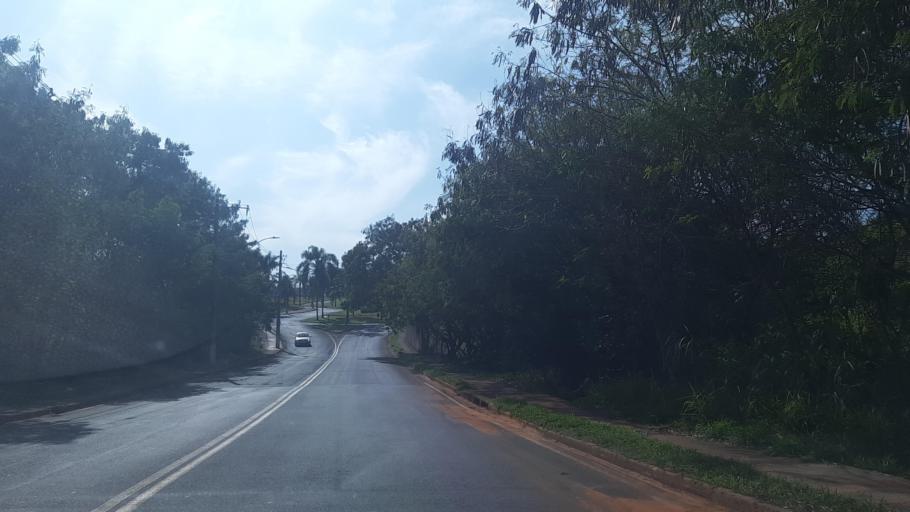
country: BR
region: Minas Gerais
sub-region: Uberlandia
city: Uberlandia
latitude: -18.8779
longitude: -48.2382
